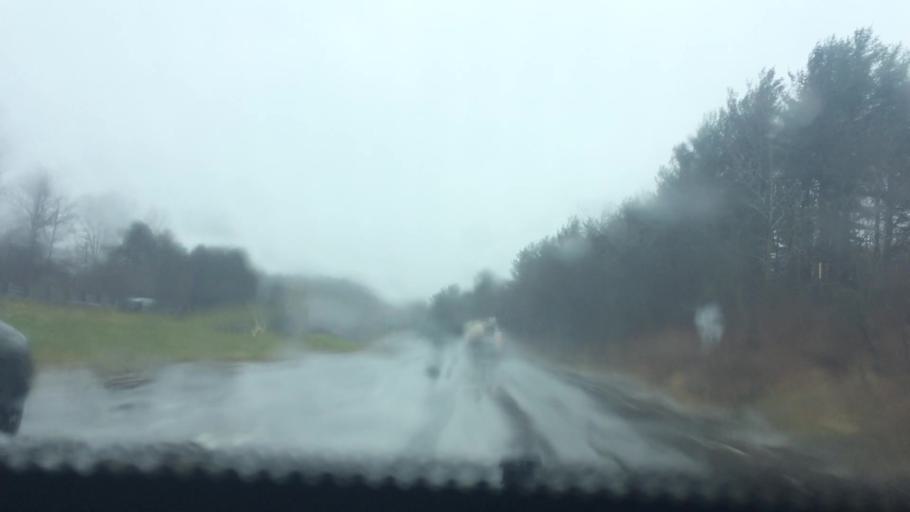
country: US
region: Massachusetts
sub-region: Essex County
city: Haverhill
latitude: 42.7535
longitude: -71.1124
